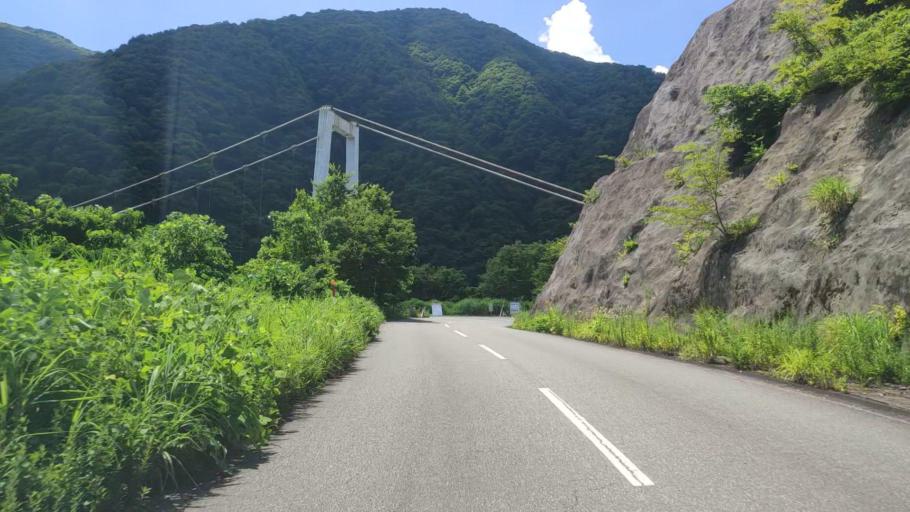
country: JP
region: Fukui
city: Ono
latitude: 35.8968
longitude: 136.5255
